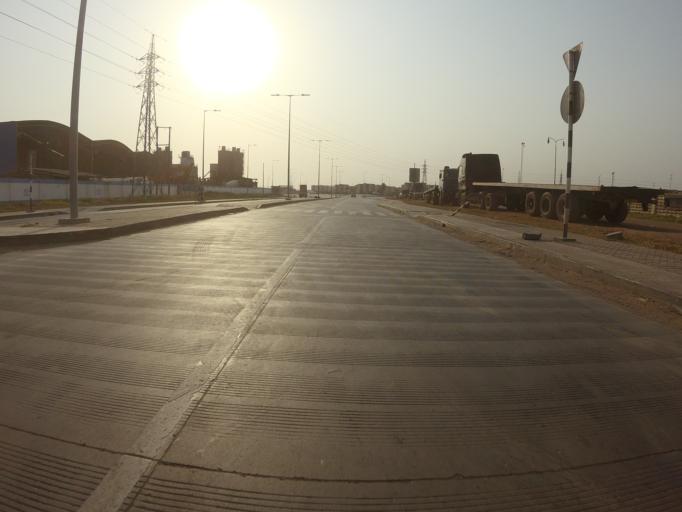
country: GH
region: Greater Accra
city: Tema
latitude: 5.6173
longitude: -0.0209
